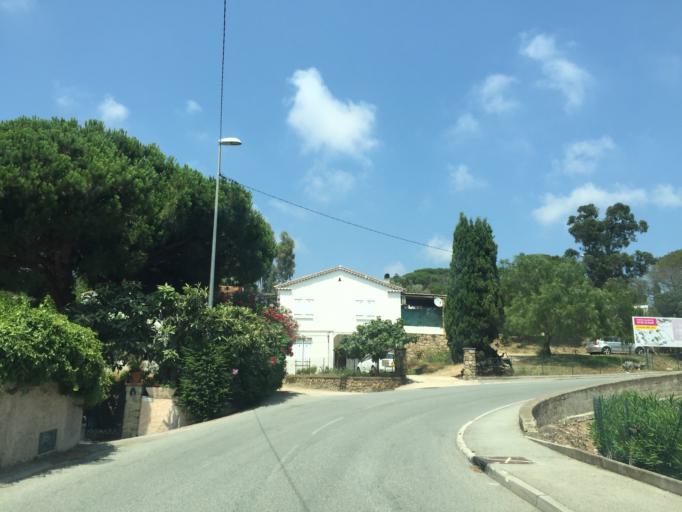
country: FR
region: Provence-Alpes-Cote d'Azur
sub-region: Departement du Var
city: Sainte-Maxime
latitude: 43.3440
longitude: 6.6766
